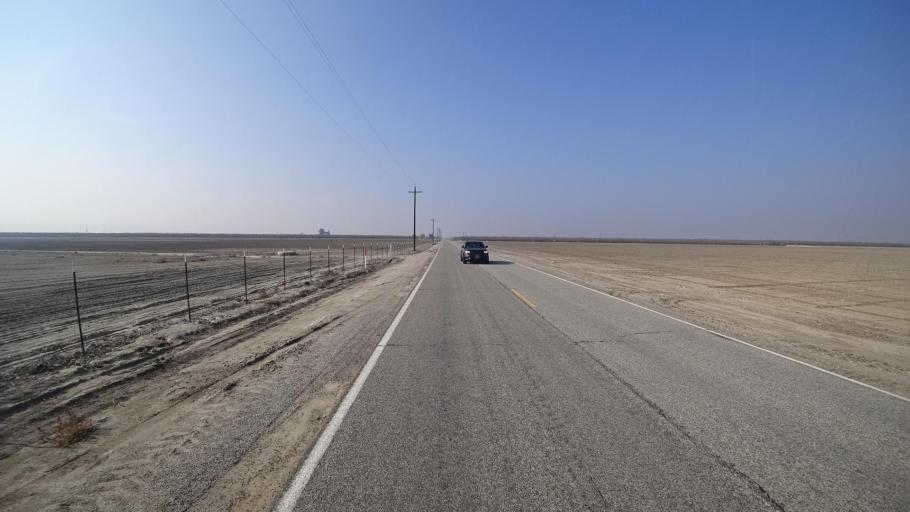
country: US
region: California
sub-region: Kern County
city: Buttonwillow
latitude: 35.3548
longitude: -119.3728
